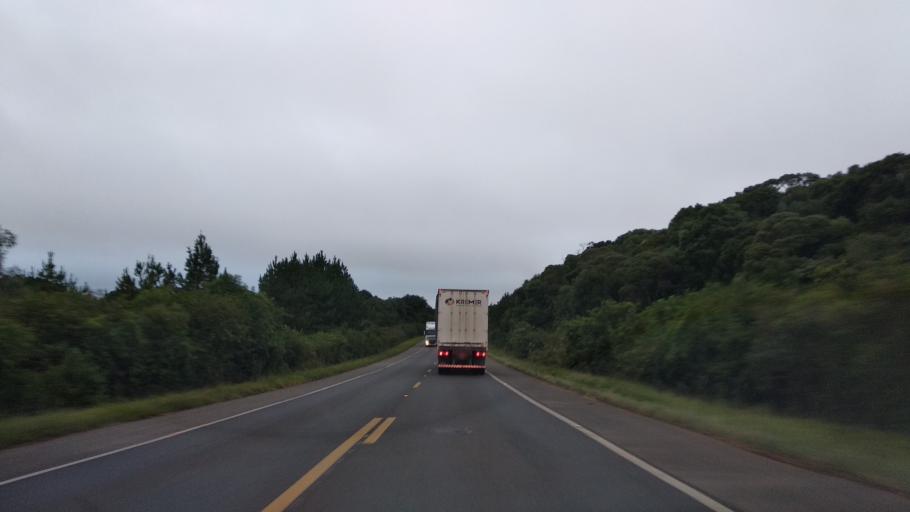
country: BR
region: Santa Catarina
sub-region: Campos Novos
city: Campos Novos
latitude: -27.3774
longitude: -51.0929
